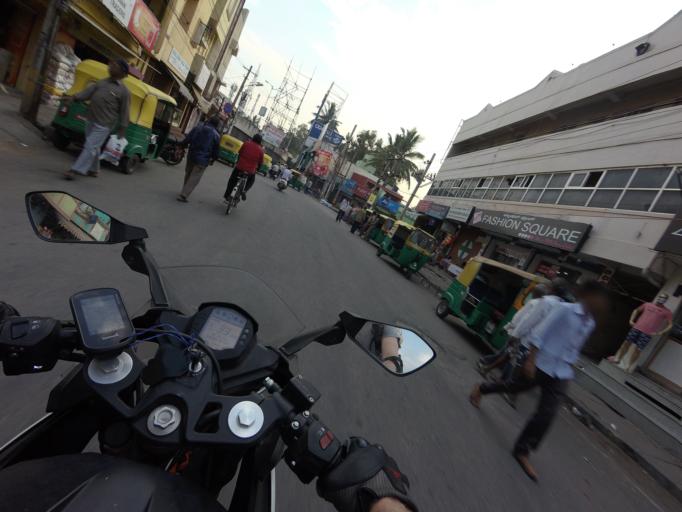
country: IN
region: Karnataka
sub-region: Bangalore Urban
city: Bangalore
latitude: 13.0050
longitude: 77.6361
